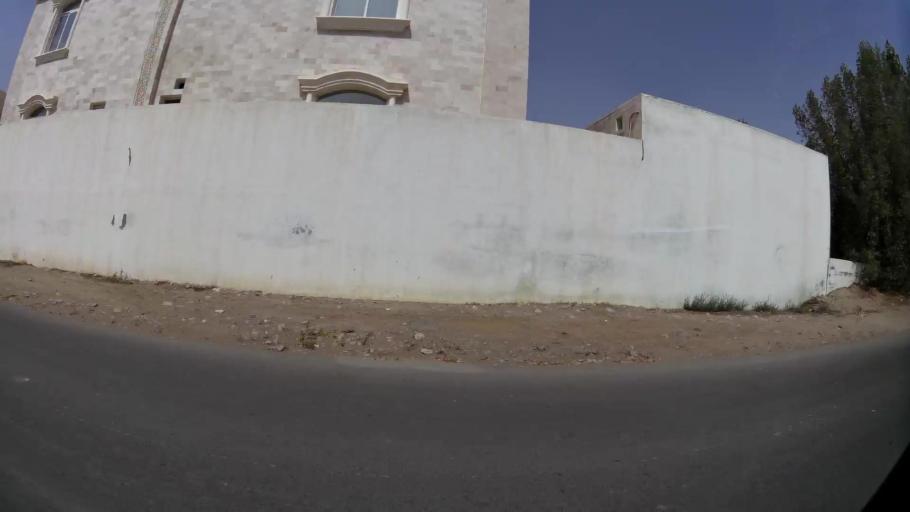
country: OM
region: Muhafazat Masqat
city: Bawshar
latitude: 23.5816
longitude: 58.4063
